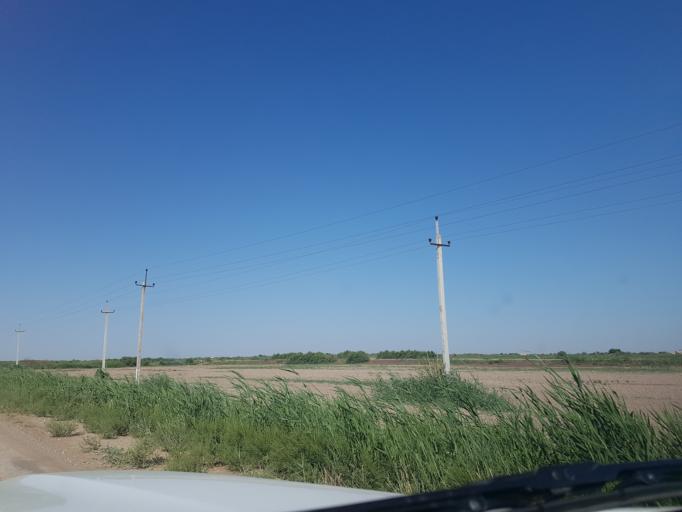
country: TM
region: Dasoguz
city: Koeneuergench
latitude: 42.1313
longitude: 58.9471
